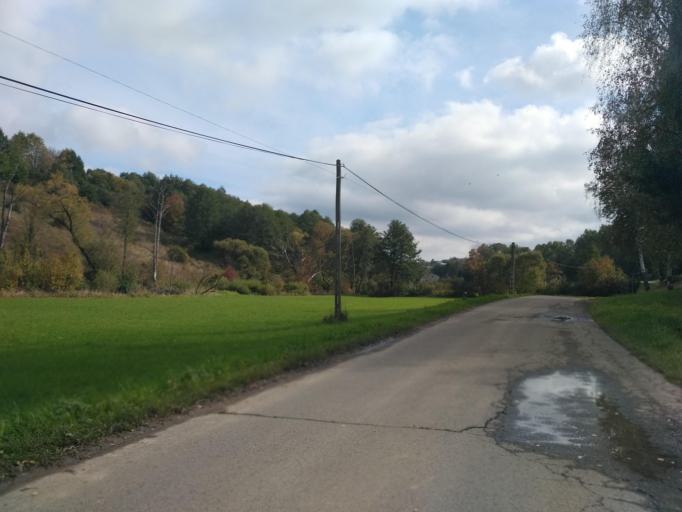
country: PL
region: Subcarpathian Voivodeship
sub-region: Powiat ropczycko-sedziszowski
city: Niedzwiada
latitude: 49.9355
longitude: 21.5324
